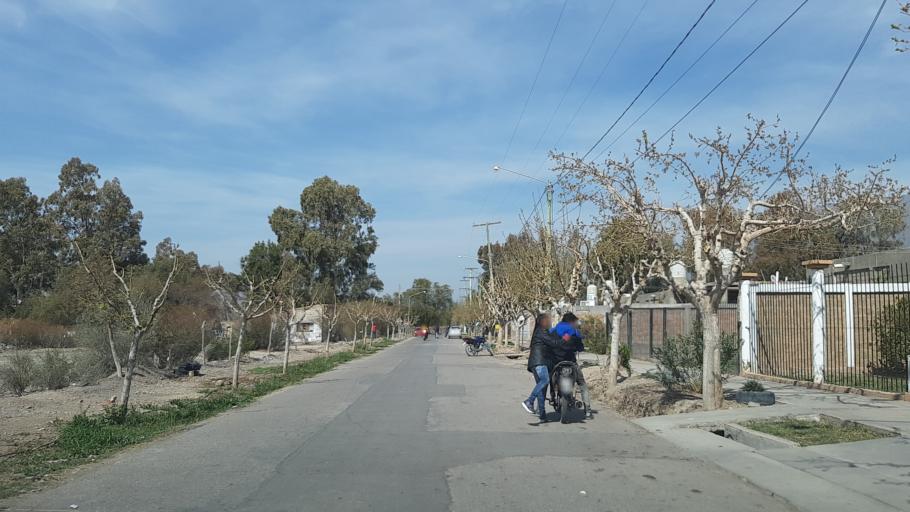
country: AR
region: San Juan
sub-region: Departamento de Zonda
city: Zonda
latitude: -31.5414
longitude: -68.7508
